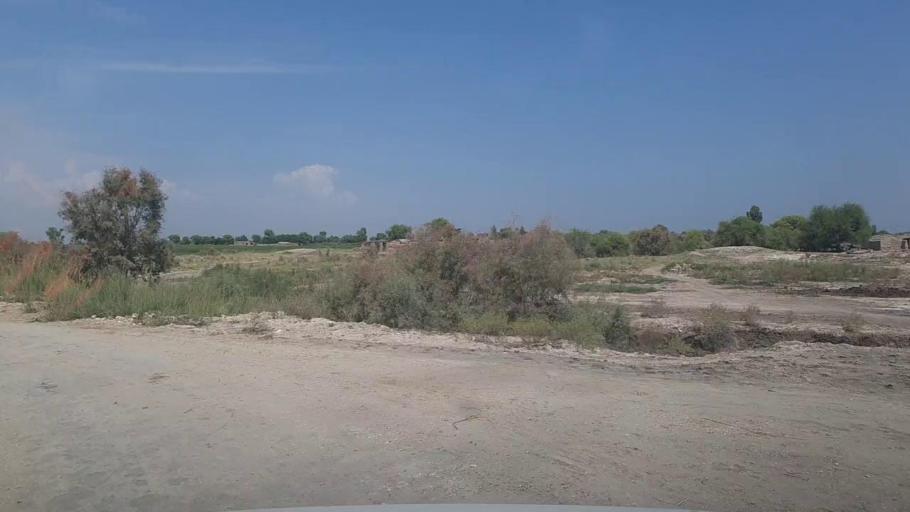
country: PK
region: Sindh
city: Kandhkot
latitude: 28.2818
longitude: 69.2380
